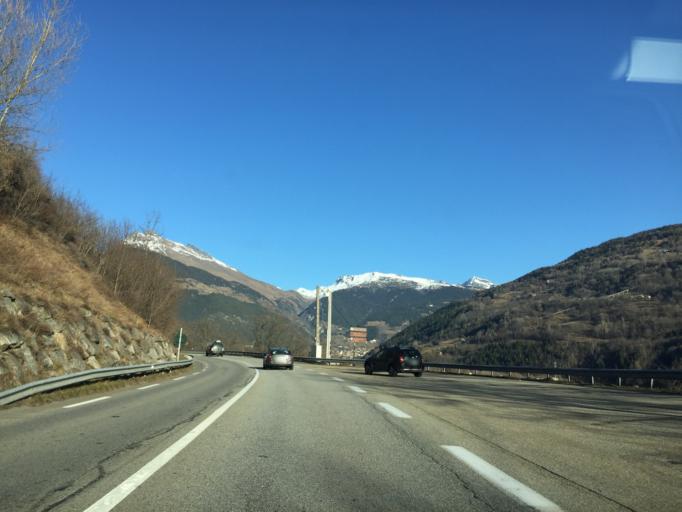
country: FR
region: Rhone-Alpes
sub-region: Departement de la Savoie
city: Bourg-Saint-Maurice
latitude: 45.6031
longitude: 6.7549
